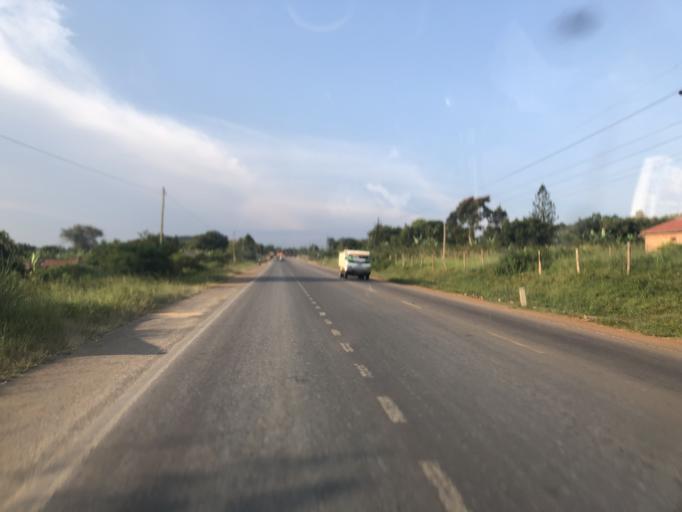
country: UG
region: Central Region
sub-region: Mpigi District
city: Mpigi
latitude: 0.1679
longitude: 32.2586
